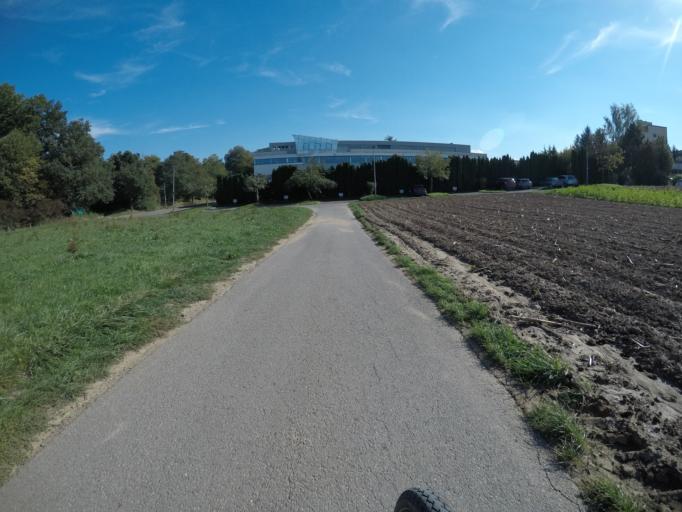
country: DE
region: Baden-Wuerttemberg
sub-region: Regierungsbezirk Stuttgart
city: Steinenbronn
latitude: 48.6948
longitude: 9.1299
